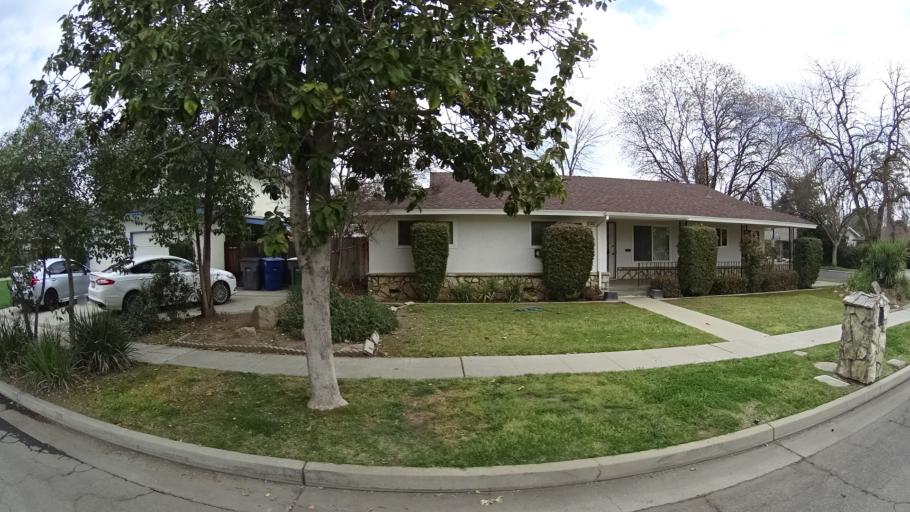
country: US
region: California
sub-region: Fresno County
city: Clovis
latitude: 36.8205
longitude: -119.7599
